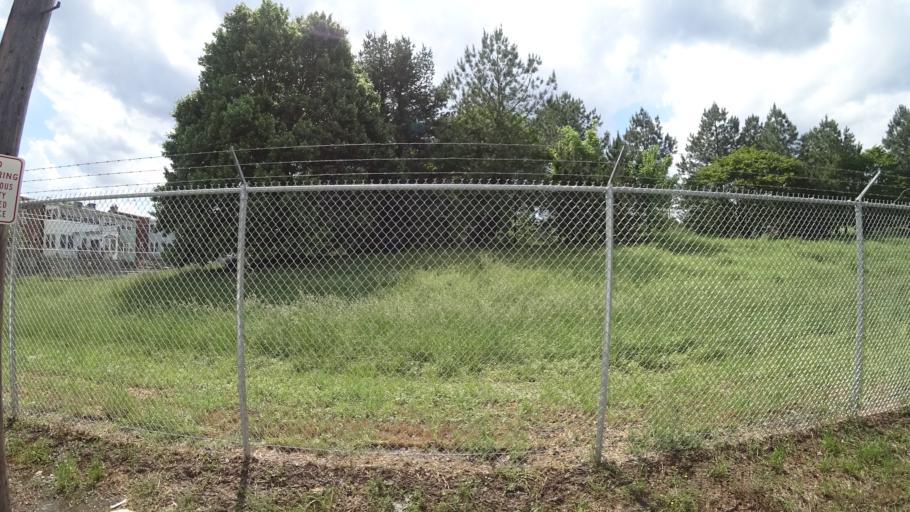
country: US
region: Maryland
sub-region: Prince George's County
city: Mount Rainier
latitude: 38.9356
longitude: -76.9819
